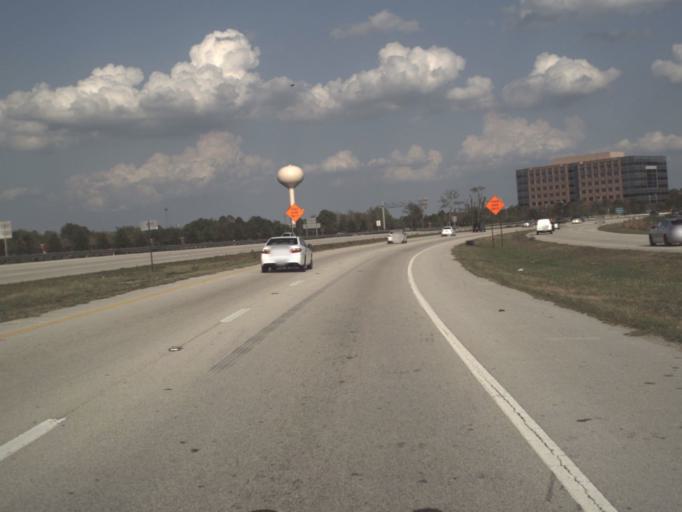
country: US
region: Florida
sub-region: Orange County
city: Lockhart
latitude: 28.6406
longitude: -81.4108
